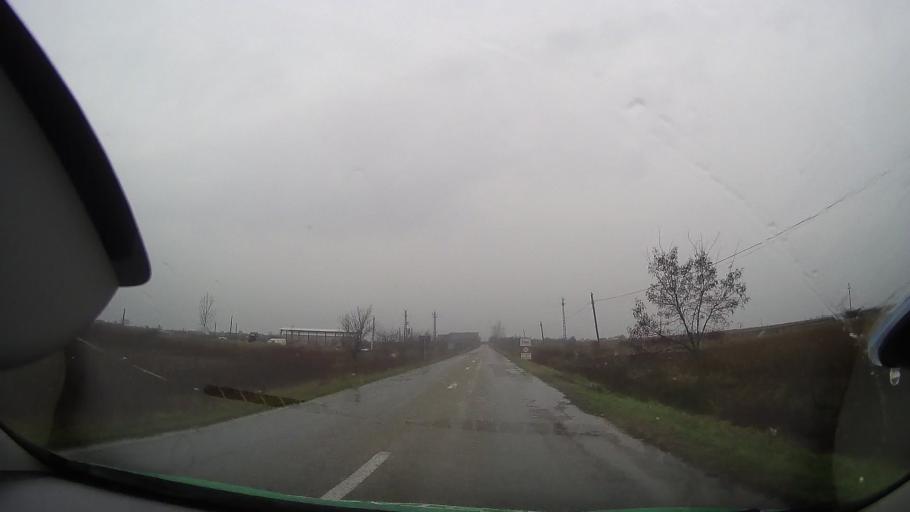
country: RO
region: Bihor
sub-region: Comuna Tulca
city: Tulca
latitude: 46.7855
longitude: 21.7935
